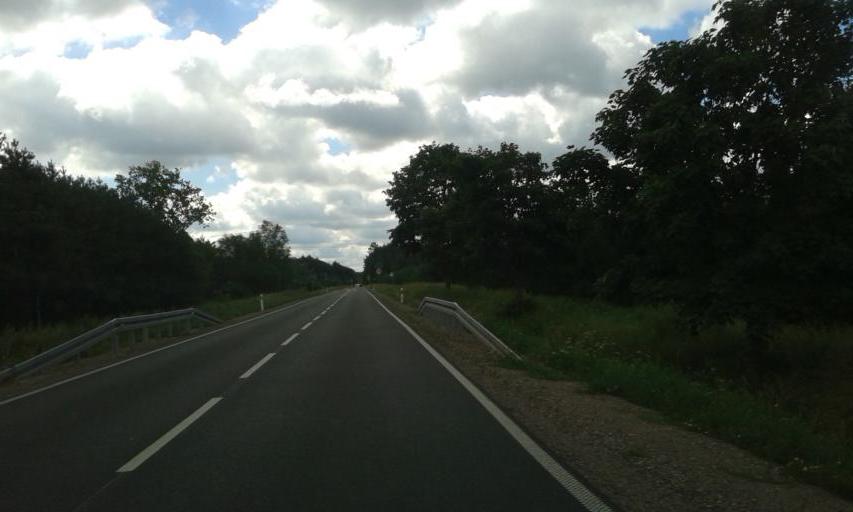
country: PL
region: West Pomeranian Voivodeship
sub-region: Powiat szczecinecki
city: Lubowo
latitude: 53.4768
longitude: 16.3561
